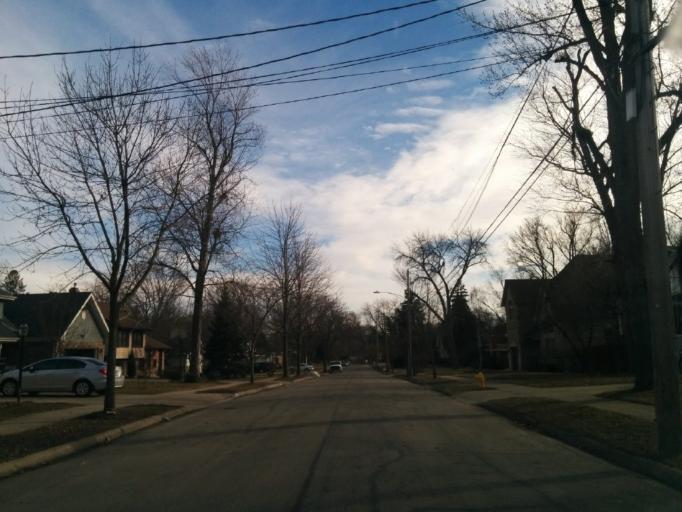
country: US
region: Illinois
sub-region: DuPage County
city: Villa Park
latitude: 41.8880
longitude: -87.9987
